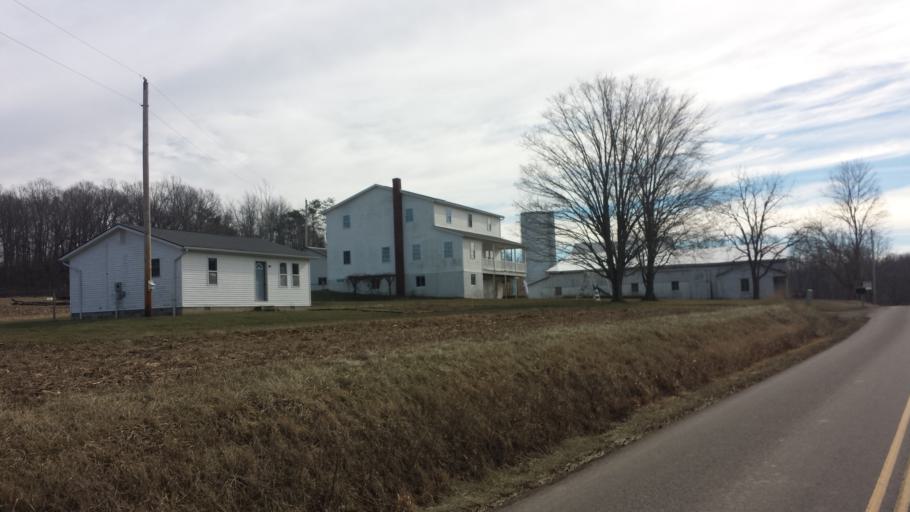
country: US
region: Ohio
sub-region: Gallia County
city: Gallipolis
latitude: 38.7300
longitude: -82.3670
